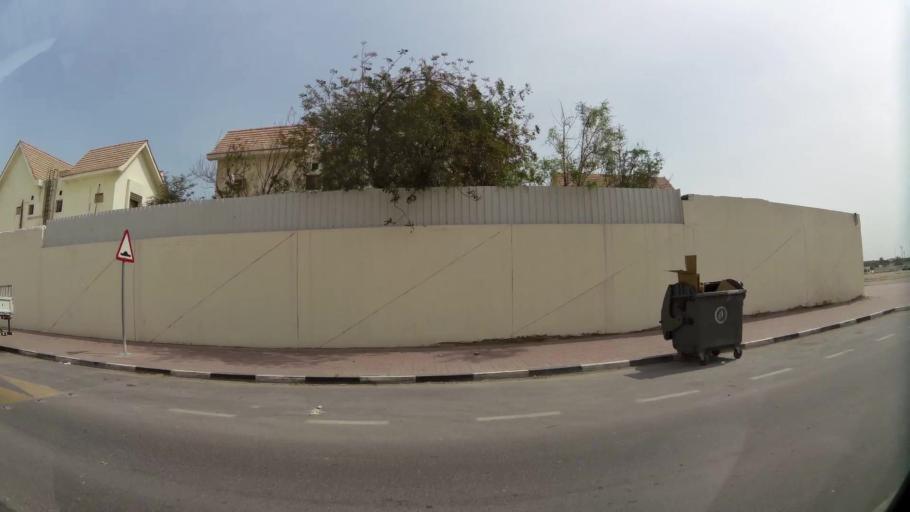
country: QA
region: Baladiyat ad Dawhah
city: Doha
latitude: 25.2665
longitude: 51.4865
